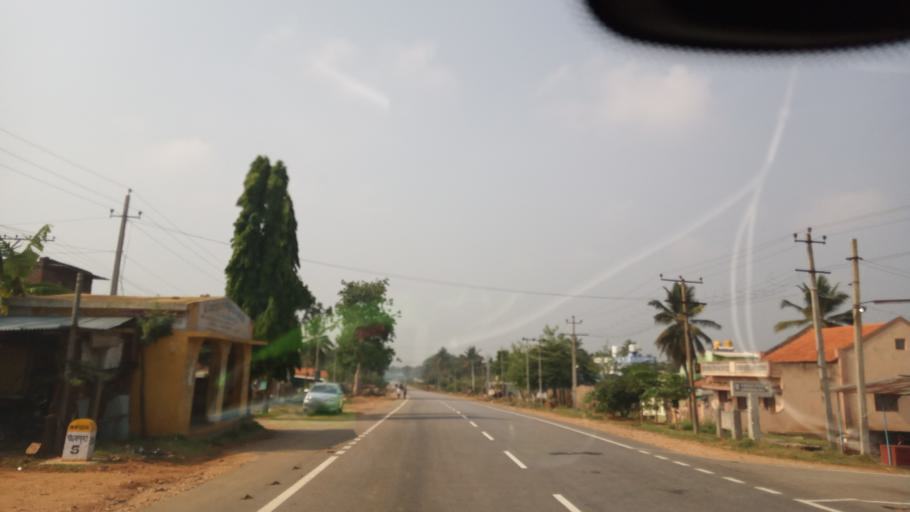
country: IN
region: Karnataka
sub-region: Mandya
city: Pandavapura
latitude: 12.5507
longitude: 76.6718
